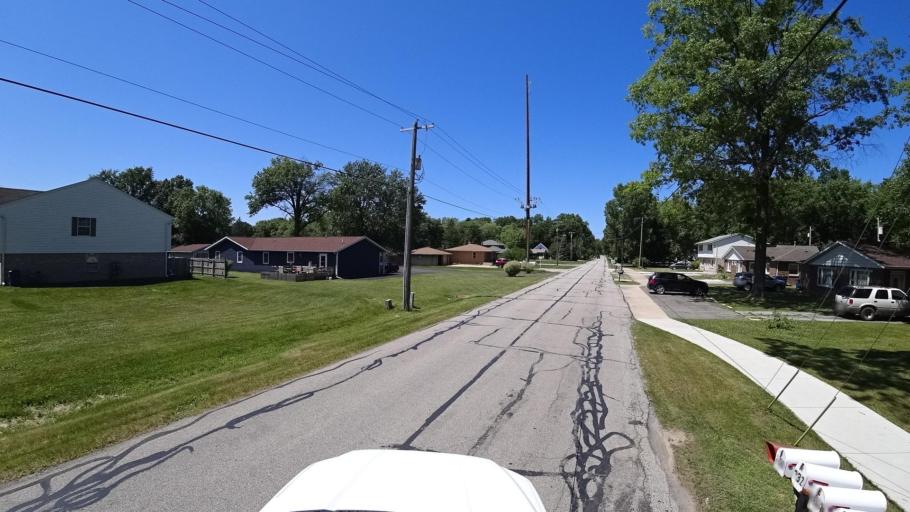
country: US
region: Indiana
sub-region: Porter County
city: Porter
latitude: 41.6010
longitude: -87.0814
